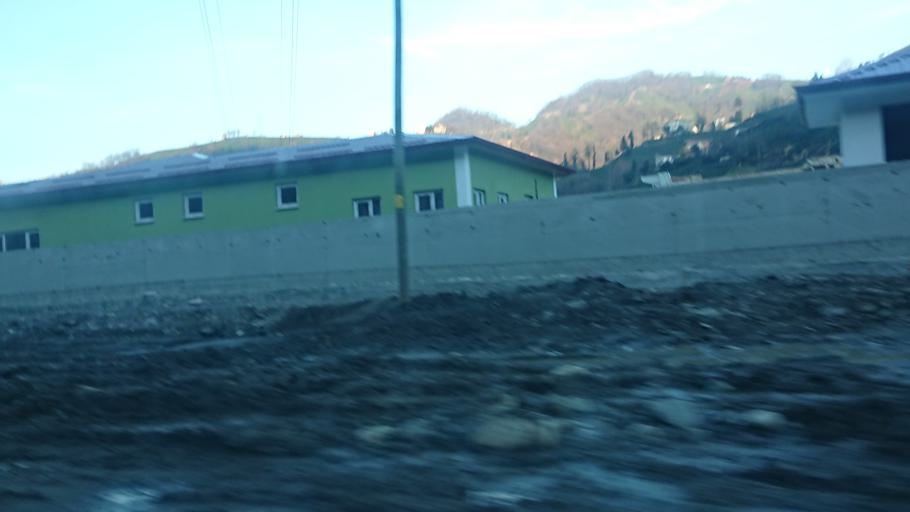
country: TR
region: Rize
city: Gundogdu
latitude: 41.0236
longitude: 40.5768
